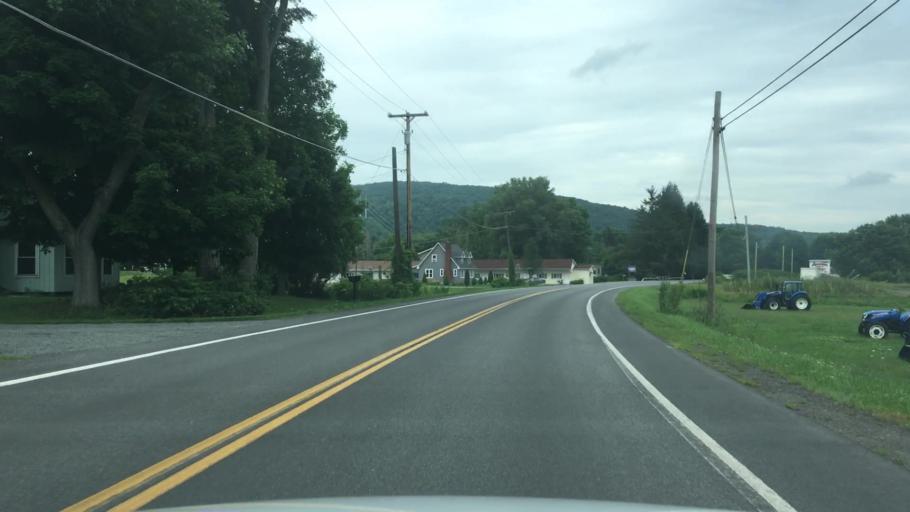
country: US
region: New York
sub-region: Otsego County
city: Otego
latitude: 42.4210
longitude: -75.1424
